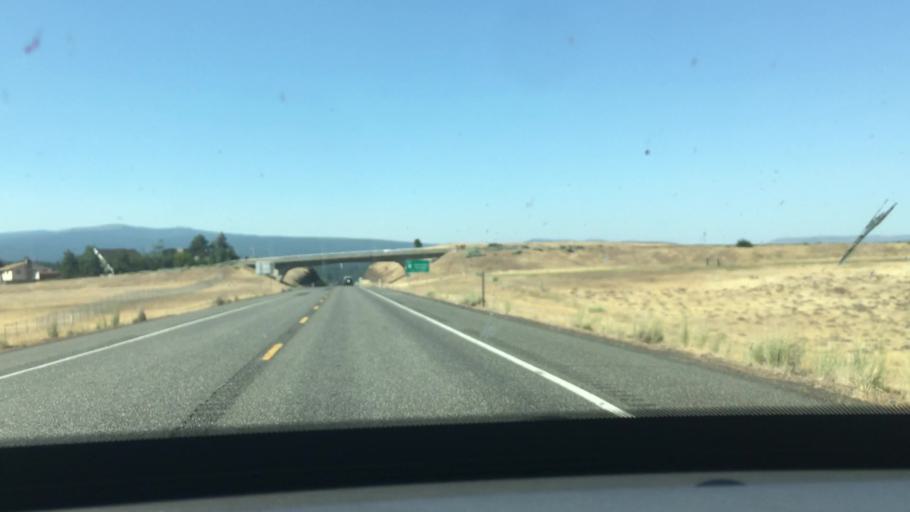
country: US
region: Washington
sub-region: Klickitat County
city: Goldendale
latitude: 45.8165
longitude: -120.8063
